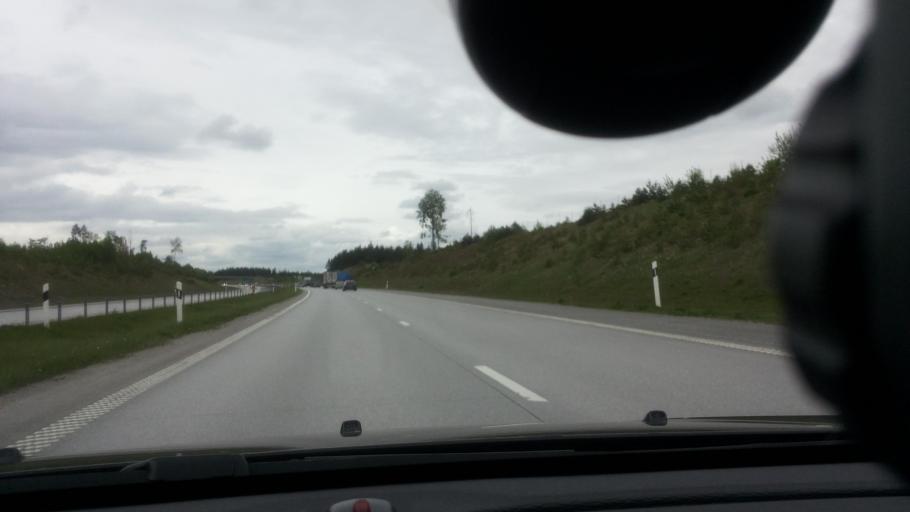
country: SE
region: Uppsala
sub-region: Uppsala Kommun
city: Gamla Uppsala
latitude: 59.9259
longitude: 17.6578
